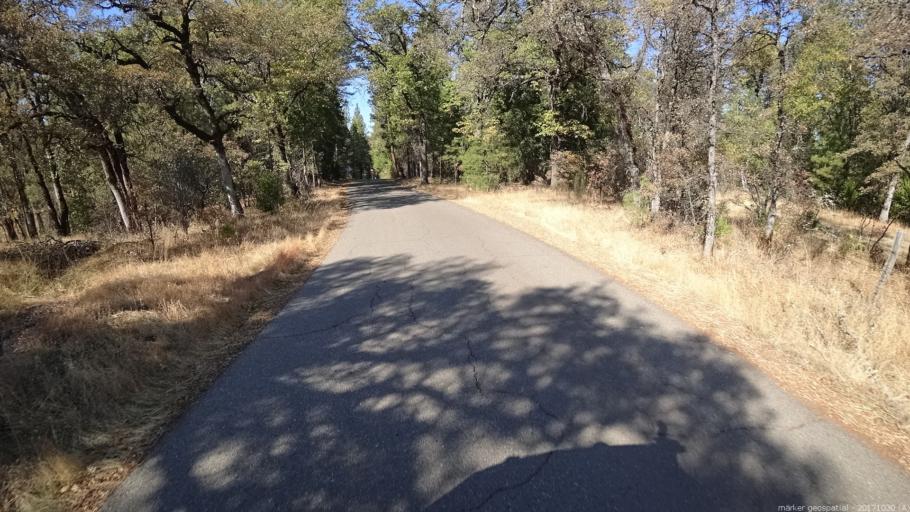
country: US
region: California
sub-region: Shasta County
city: Shingletown
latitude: 40.5288
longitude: -121.9262
